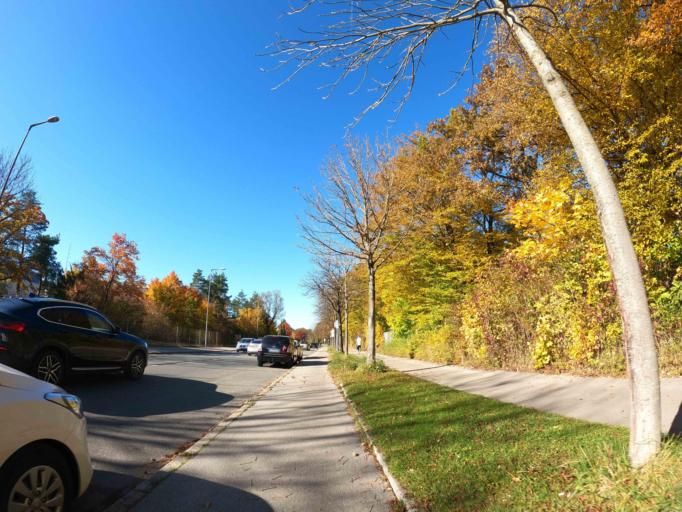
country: DE
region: Bavaria
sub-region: Upper Bavaria
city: Neubiberg
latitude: 48.0924
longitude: 11.6578
